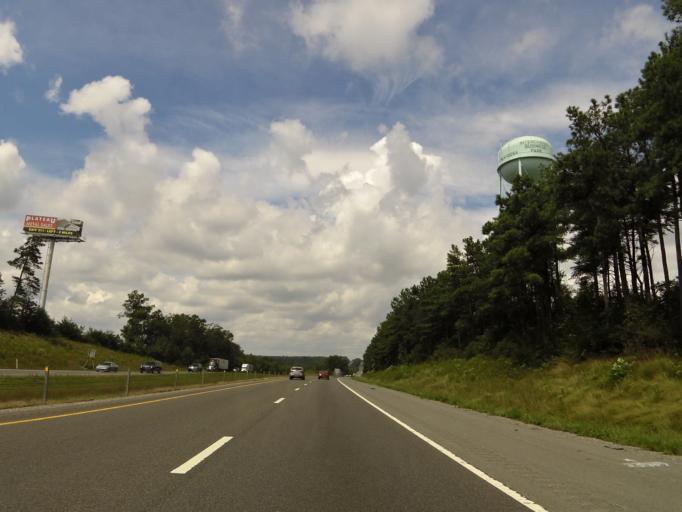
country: US
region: Tennessee
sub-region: Cumberland County
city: Crossville
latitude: 36.0061
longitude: -85.0554
